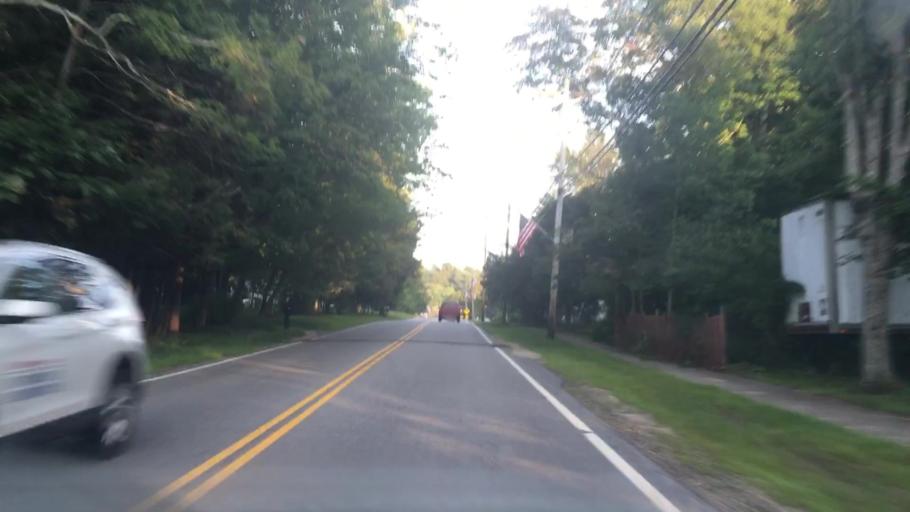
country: US
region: New Hampshire
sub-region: Belknap County
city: Barnstead
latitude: 43.4195
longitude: -71.2997
